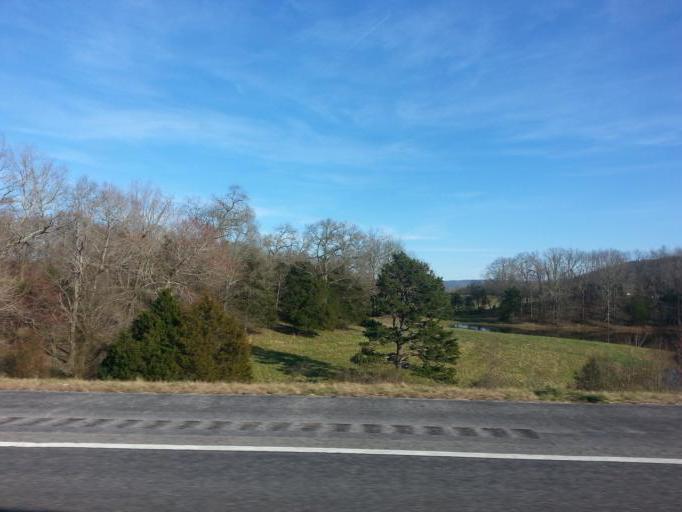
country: US
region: Tennessee
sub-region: Van Buren County
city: Spencer
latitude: 35.7628
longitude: -85.6278
